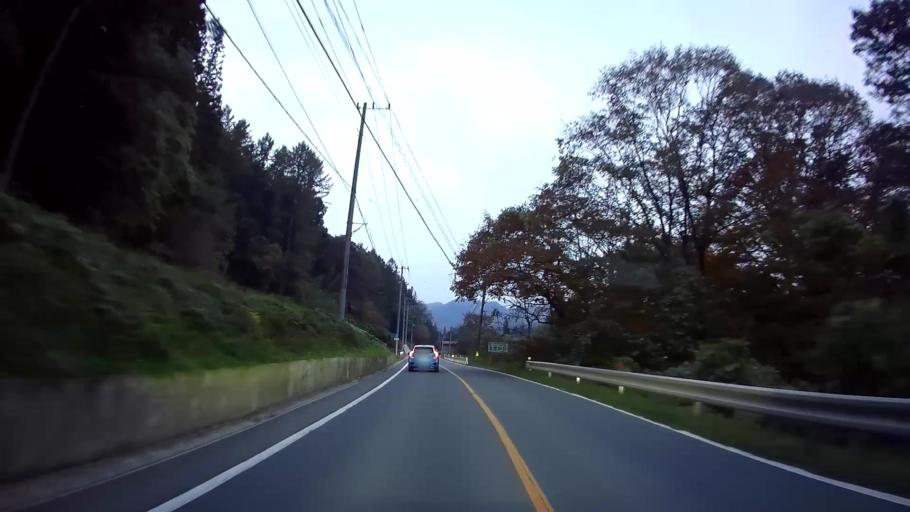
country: JP
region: Gunma
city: Nakanojomachi
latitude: 36.5405
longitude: 138.7912
